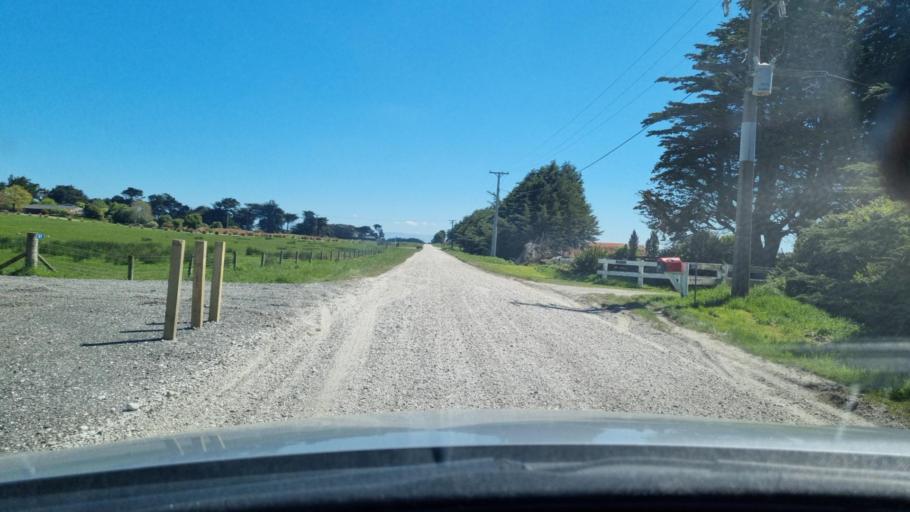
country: NZ
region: Southland
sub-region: Invercargill City
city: Invercargill
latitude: -46.4204
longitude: 168.2730
